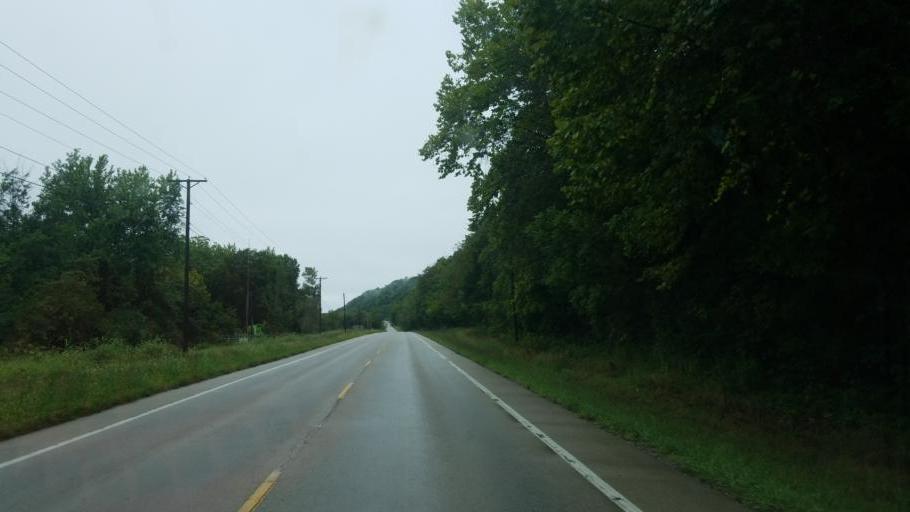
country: US
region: Kentucky
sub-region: Mason County
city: Maysville
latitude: 38.6455
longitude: -83.7078
